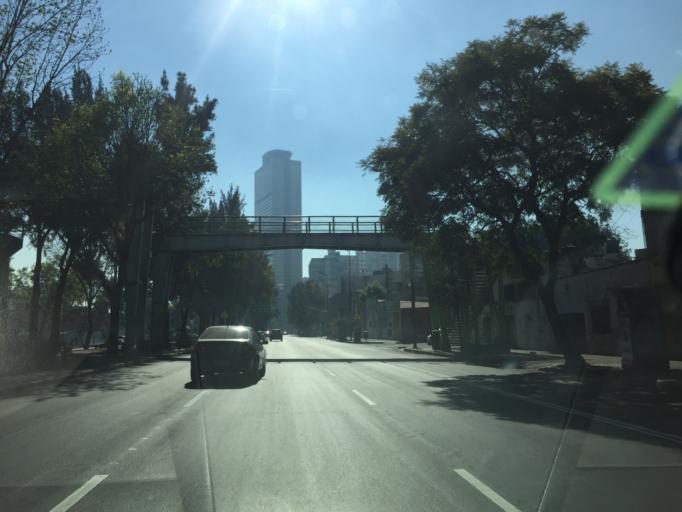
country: MX
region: Mexico City
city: Miguel Hidalgo
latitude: 19.4440
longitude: -99.1790
